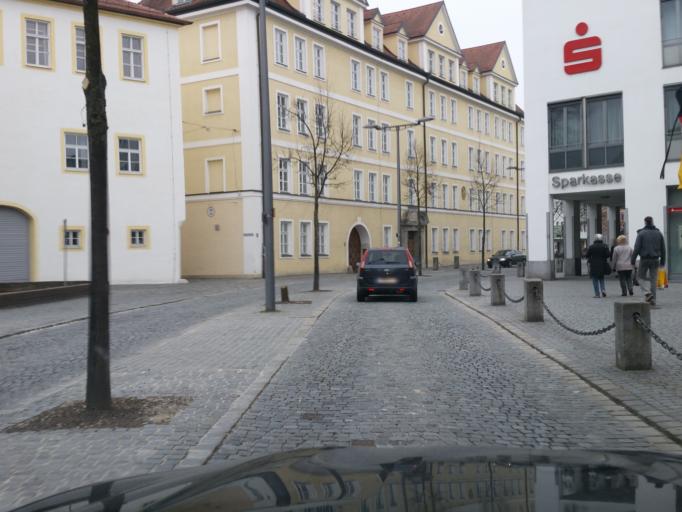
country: DE
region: Bavaria
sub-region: Lower Bavaria
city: Landshut
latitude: 48.5387
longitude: 12.1559
